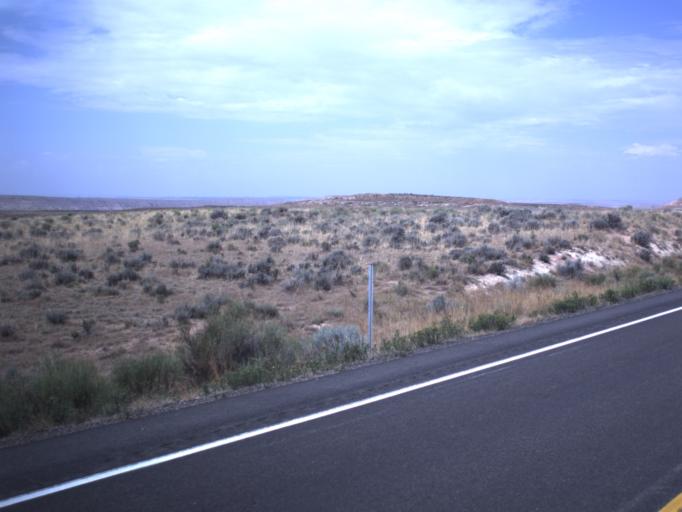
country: US
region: Utah
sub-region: Uintah County
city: Naples
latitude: 40.2609
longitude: -109.4358
